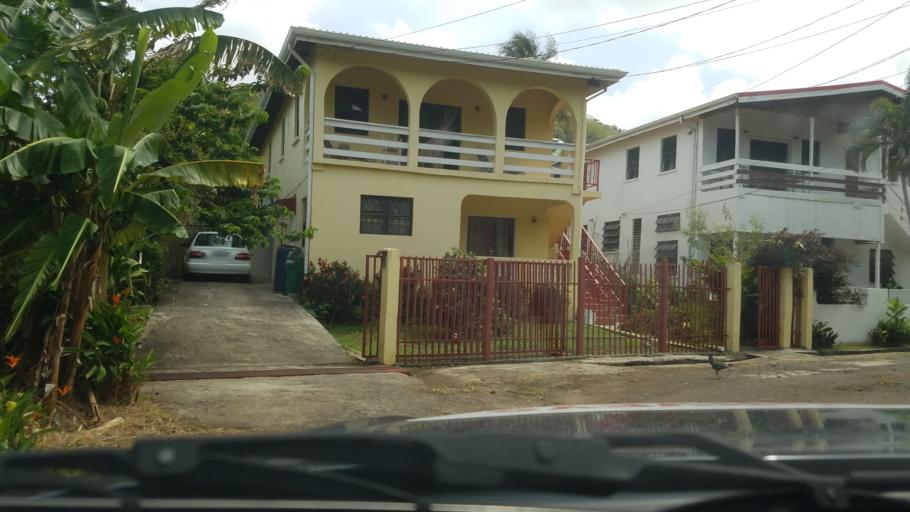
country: LC
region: Gros-Islet
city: Gros Islet
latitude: 14.0443
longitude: -60.9599
